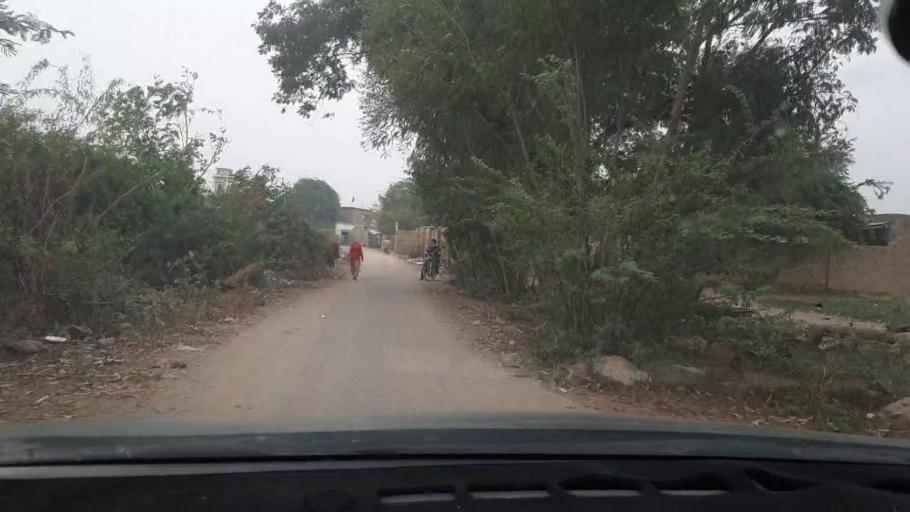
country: PK
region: Sindh
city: Malir Cantonment
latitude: 24.9232
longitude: 67.3190
